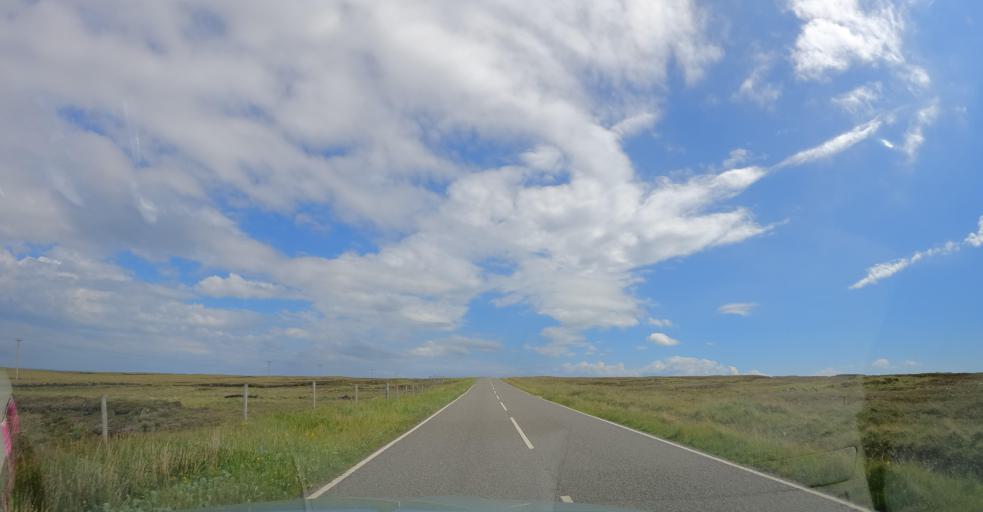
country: GB
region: Scotland
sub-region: Eilean Siar
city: Isle of Lewis
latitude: 58.4575
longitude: -6.3376
